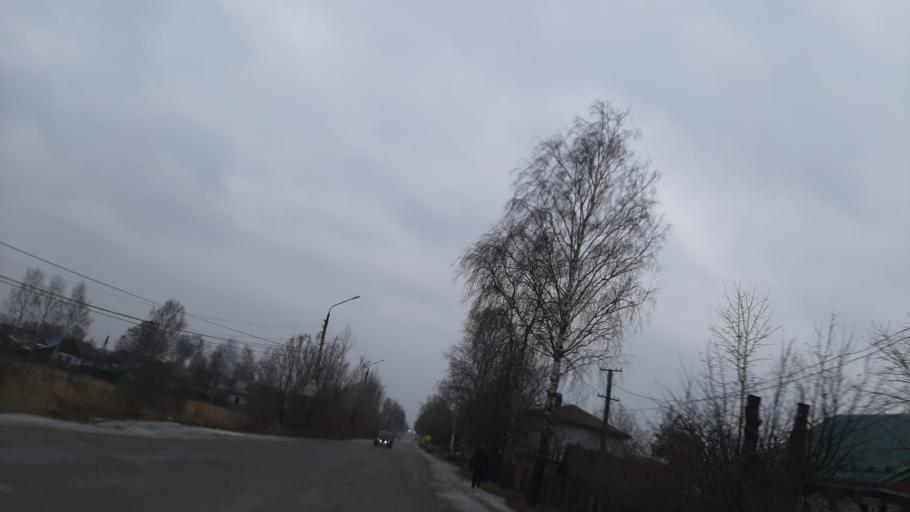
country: RU
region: Ivanovo
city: Shuya
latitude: 56.8769
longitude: 41.3481
